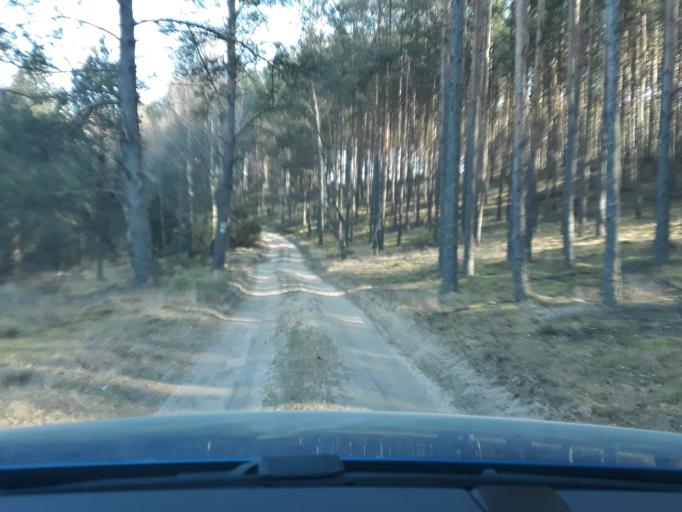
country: PL
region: Pomeranian Voivodeship
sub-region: Powiat bytowski
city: Lipnica
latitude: 53.9211
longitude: 17.4512
